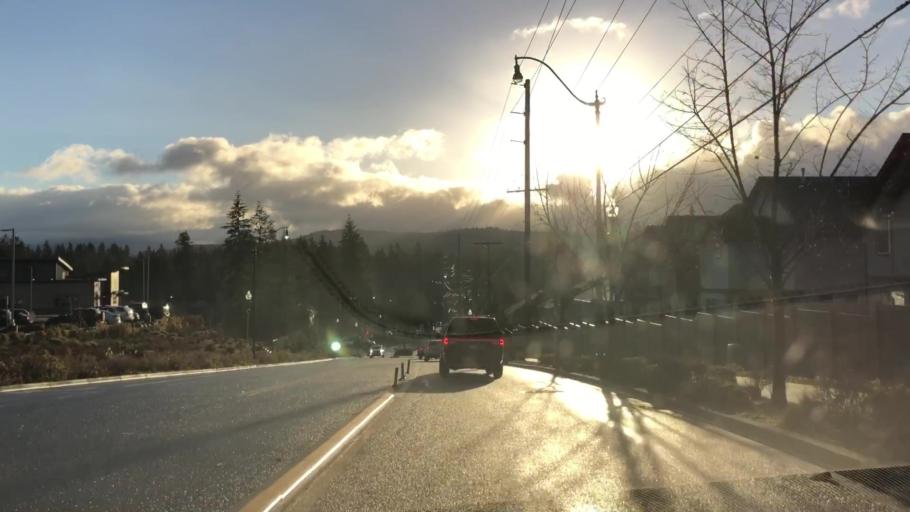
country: US
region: Washington
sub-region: King County
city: City of Sammamish
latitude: 47.5800
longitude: -122.0301
